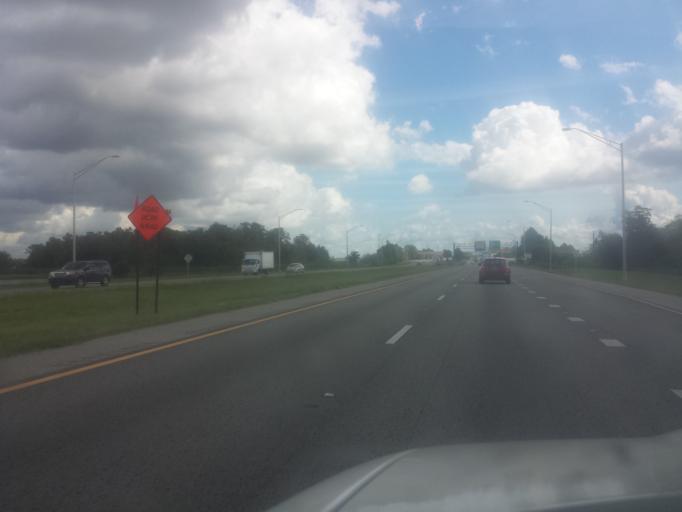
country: US
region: Florida
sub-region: Orange County
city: Meadow Woods
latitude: 28.3682
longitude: -81.3423
